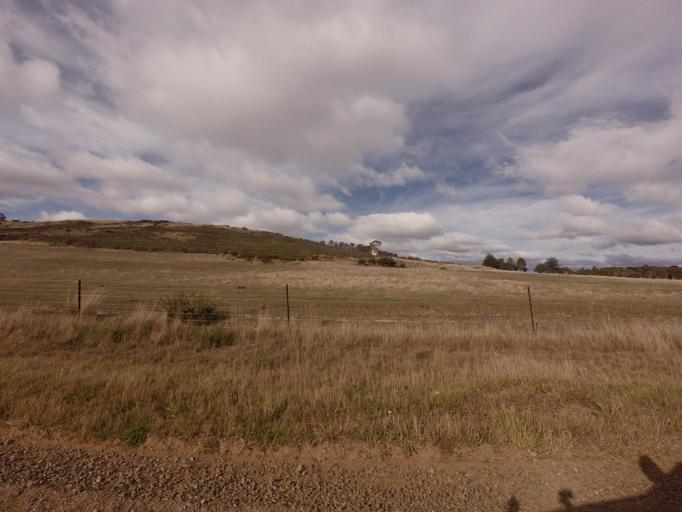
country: AU
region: Tasmania
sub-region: Brighton
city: Bridgewater
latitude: -42.4178
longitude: 147.3938
